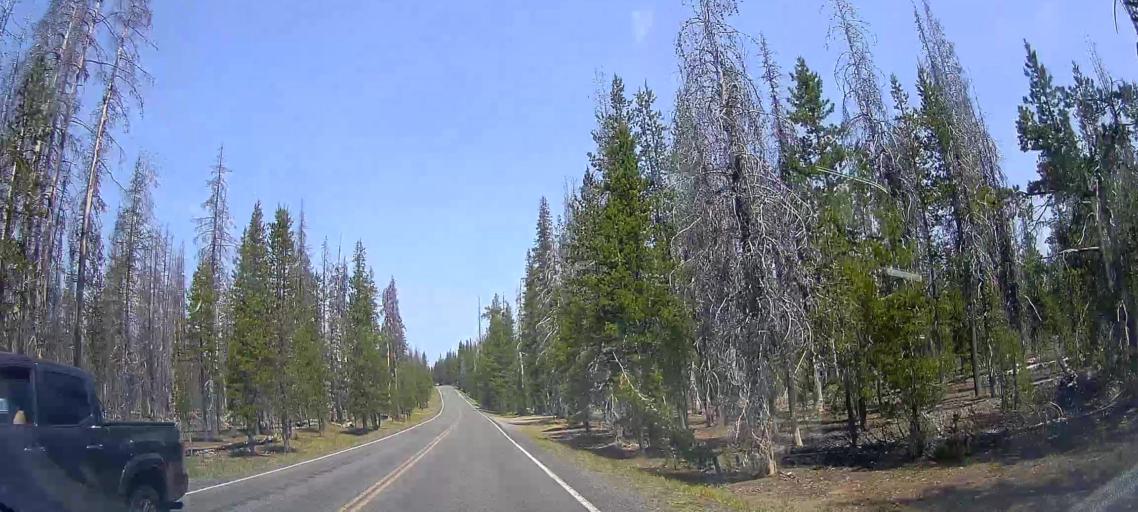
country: US
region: Oregon
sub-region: Lane County
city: Oakridge
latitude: 43.0464
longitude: -122.1191
